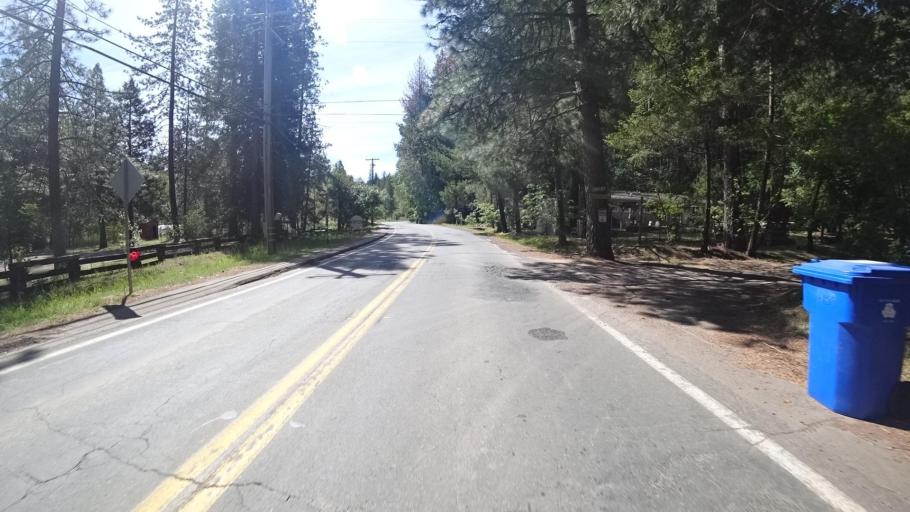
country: US
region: California
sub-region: Lake County
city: Cobb
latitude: 38.8290
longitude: -122.7295
